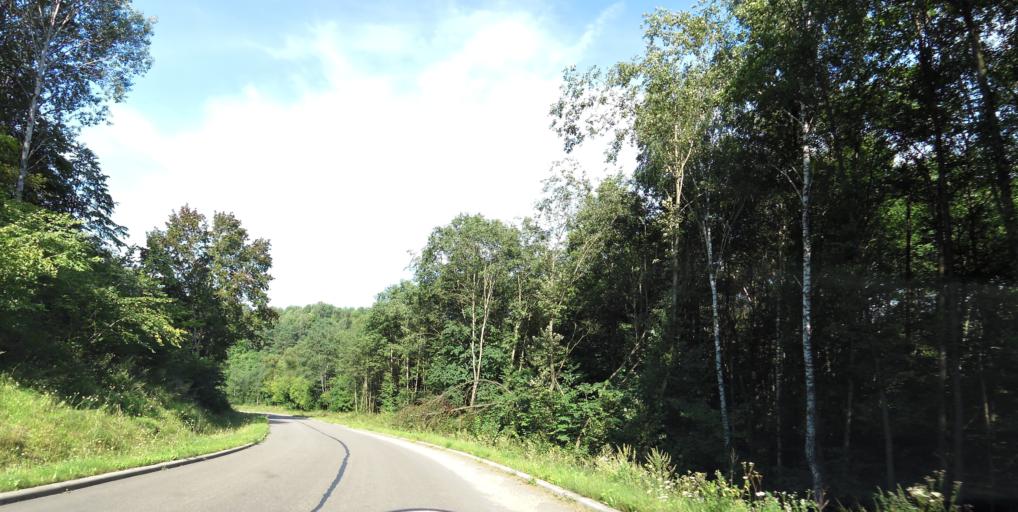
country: LT
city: Grigiskes
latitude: 54.7279
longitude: 25.0696
